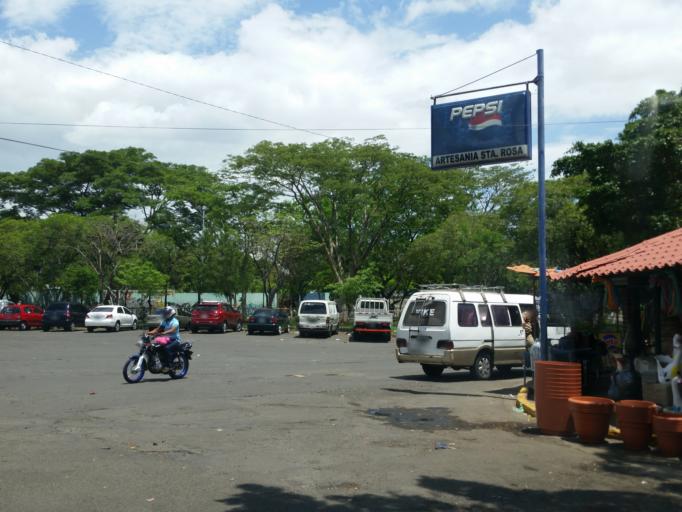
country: NI
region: Managua
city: Managua
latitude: 12.1267
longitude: -86.2432
